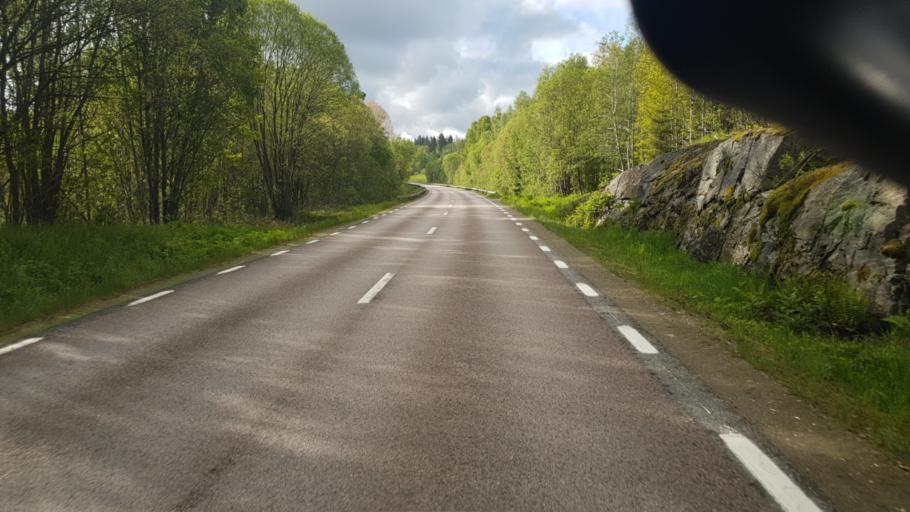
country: SE
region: Vaermland
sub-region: Eda Kommun
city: Amotfors
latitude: 59.7134
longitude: 12.2887
